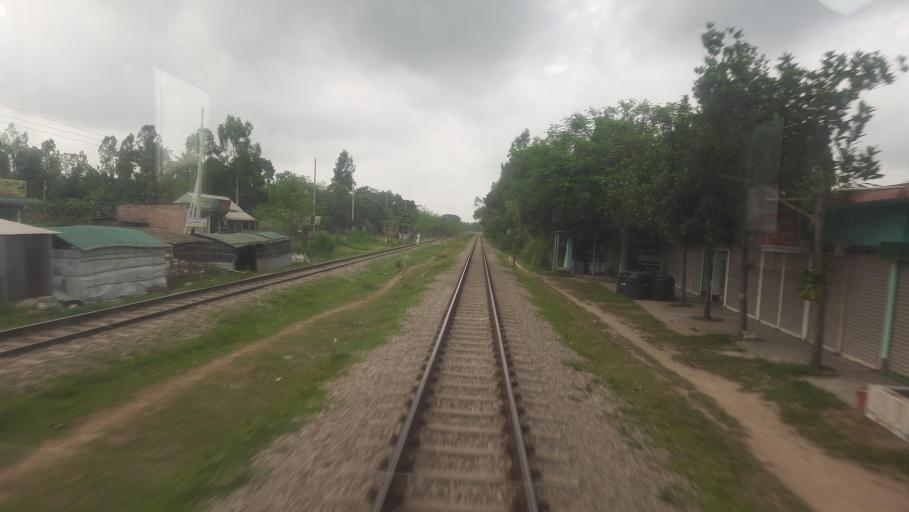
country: BD
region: Dhaka
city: Narsingdi
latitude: 23.9662
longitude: 90.8180
